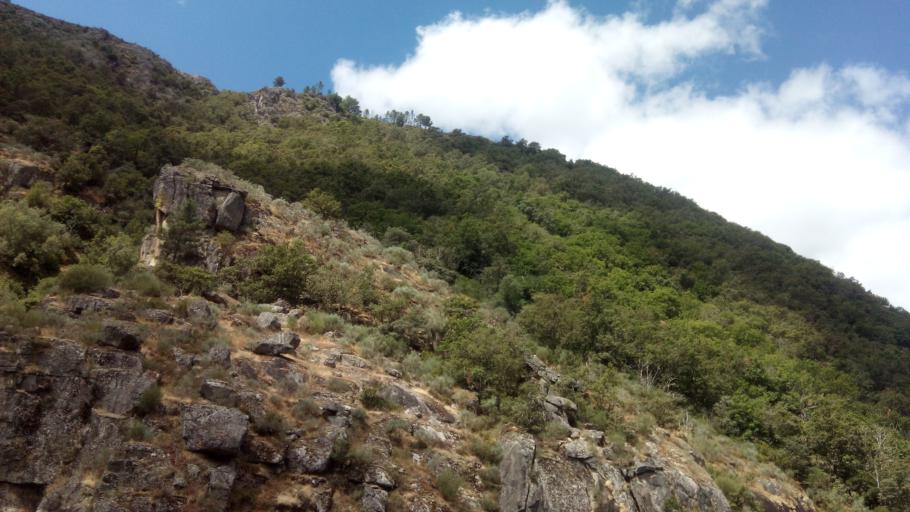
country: ES
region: Galicia
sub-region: Provincia de Lugo
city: Sober
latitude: 42.3997
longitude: -7.6289
